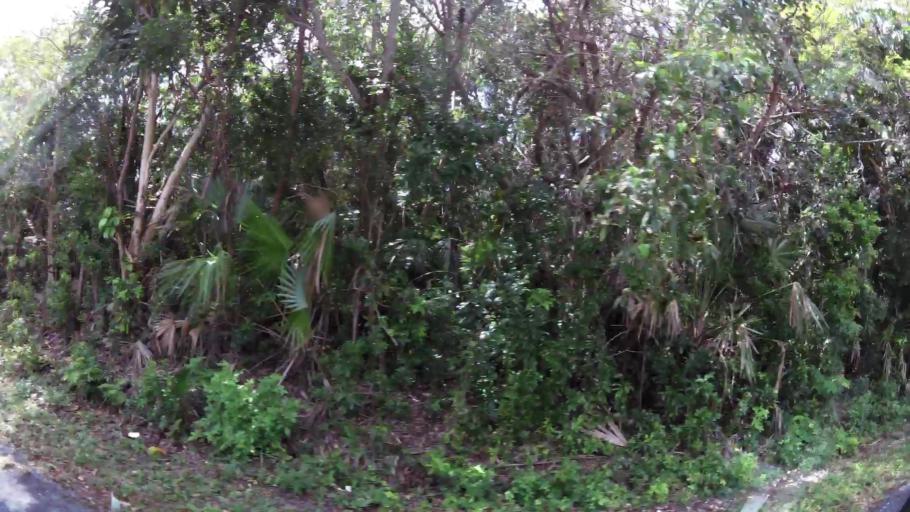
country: BS
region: Freeport
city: Lucaya
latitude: 26.5201
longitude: -78.6470
